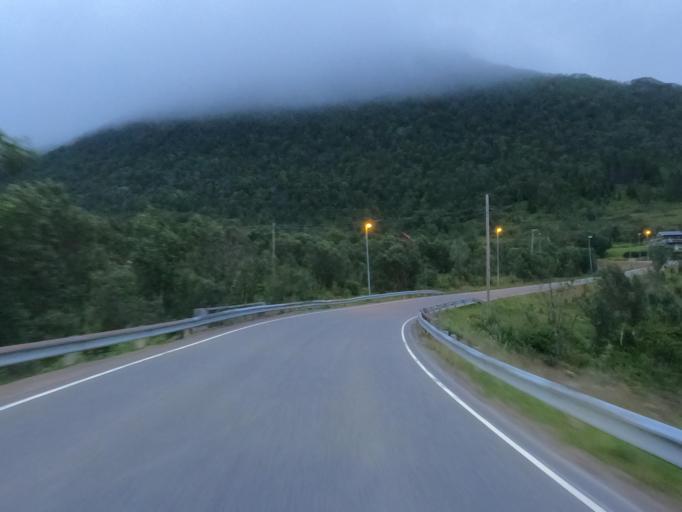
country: NO
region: Nordland
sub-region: Lodingen
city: Lodingen
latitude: 68.6160
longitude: 15.7599
